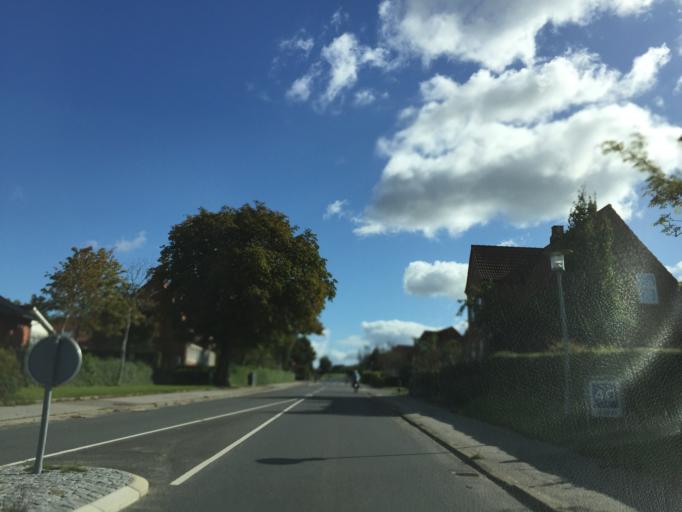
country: DK
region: Central Jutland
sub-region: Viborg Kommune
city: Viborg
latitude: 56.4470
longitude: 9.4357
